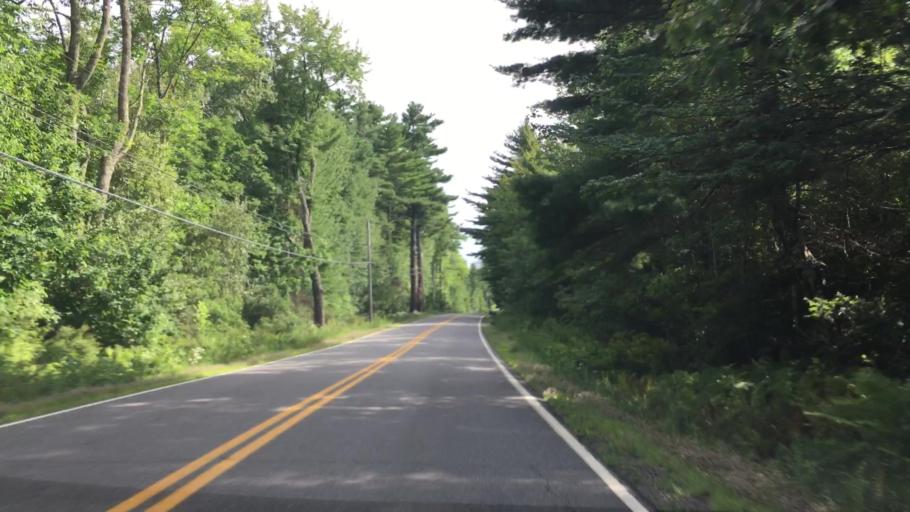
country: US
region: Maine
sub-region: Waldo County
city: Belfast
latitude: 44.3891
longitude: -69.0332
